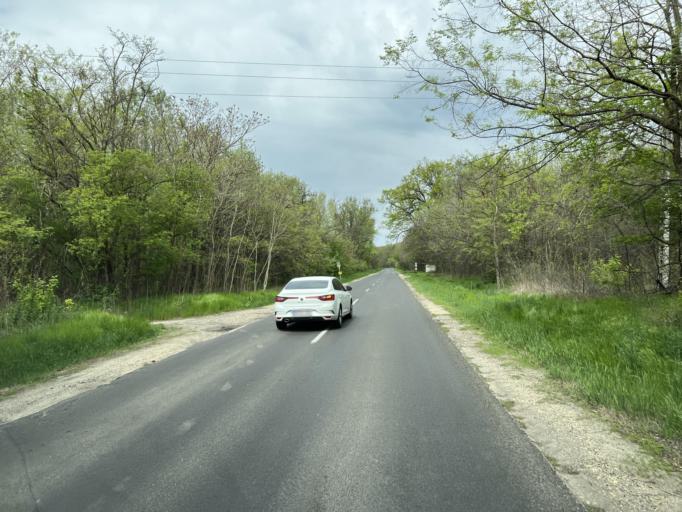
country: HU
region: Pest
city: Cegled
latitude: 47.1491
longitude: 19.8655
